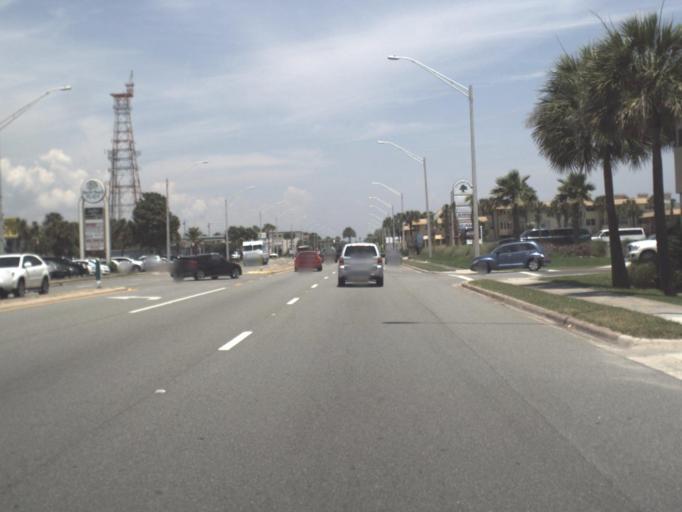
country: US
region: Florida
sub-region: Duval County
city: Jacksonville Beach
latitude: 30.3017
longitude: -81.3944
